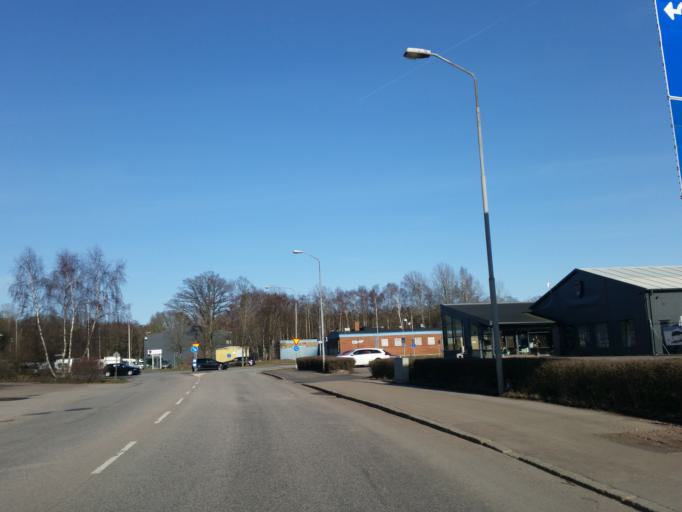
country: SE
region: Kalmar
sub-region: Kalmar Kommun
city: Kalmar
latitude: 56.6776
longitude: 16.3163
